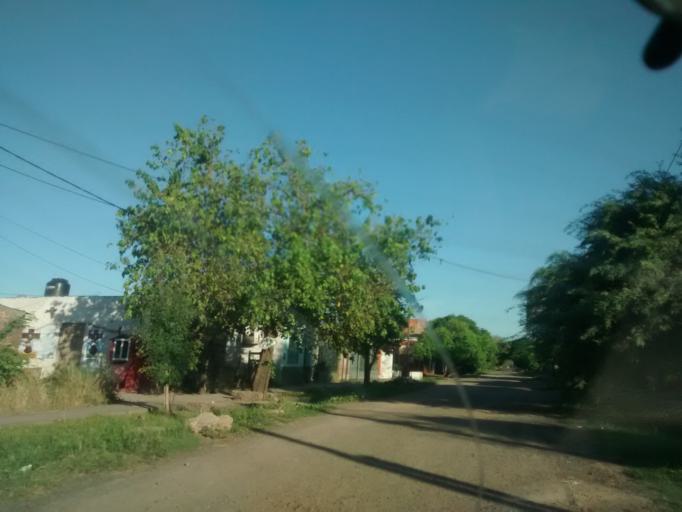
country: AR
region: Chaco
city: Resistencia
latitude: -27.4541
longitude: -59.0096
